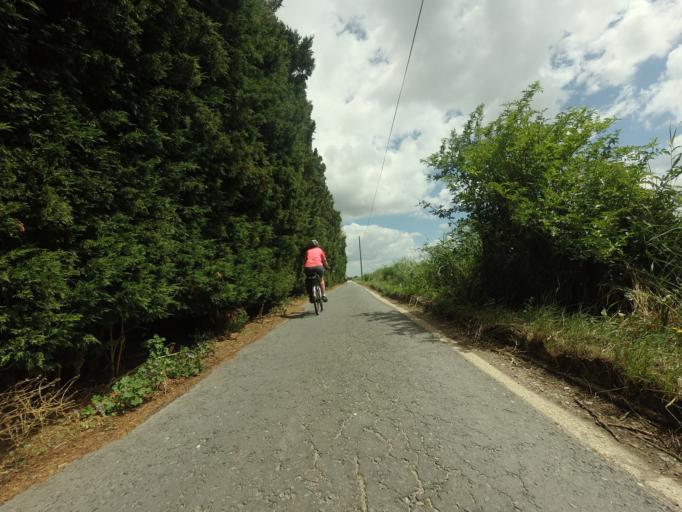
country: GB
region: England
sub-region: Kent
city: Gravesend
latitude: 51.4404
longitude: 0.4056
